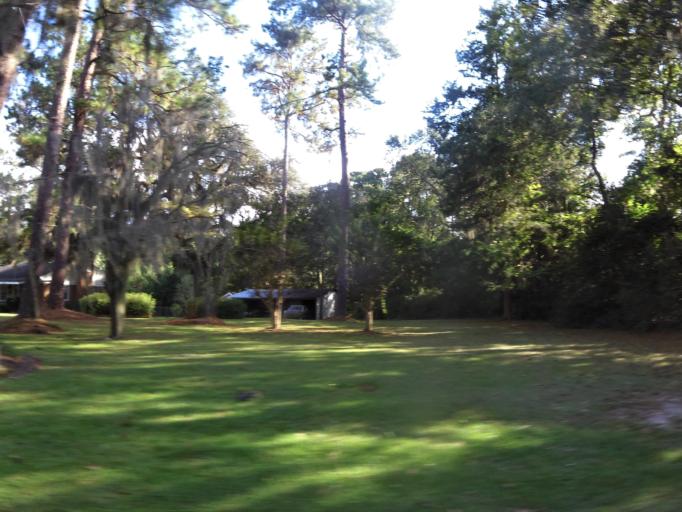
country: US
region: Georgia
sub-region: Brooks County
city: Quitman
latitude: 30.7794
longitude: -83.5530
